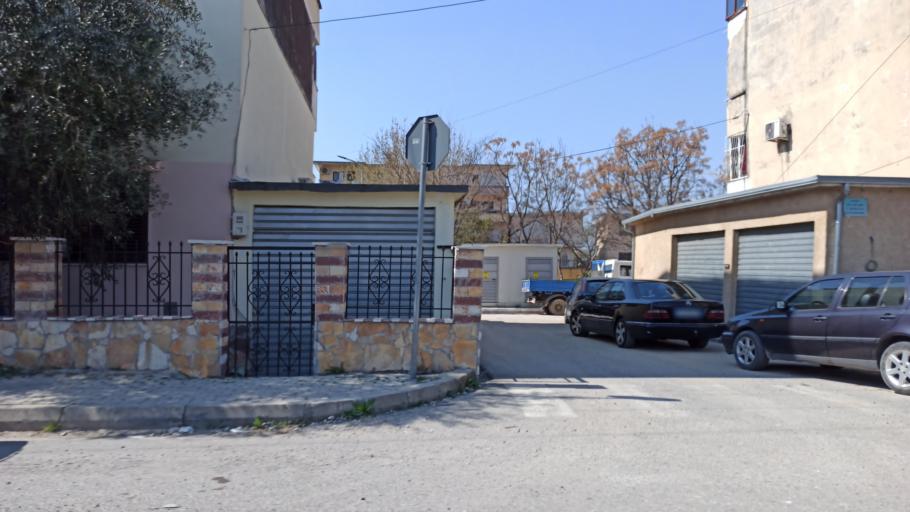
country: AL
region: Shkoder
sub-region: Rrethi i Malesia e Madhe
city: Kuc
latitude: 42.0542
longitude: 19.5229
